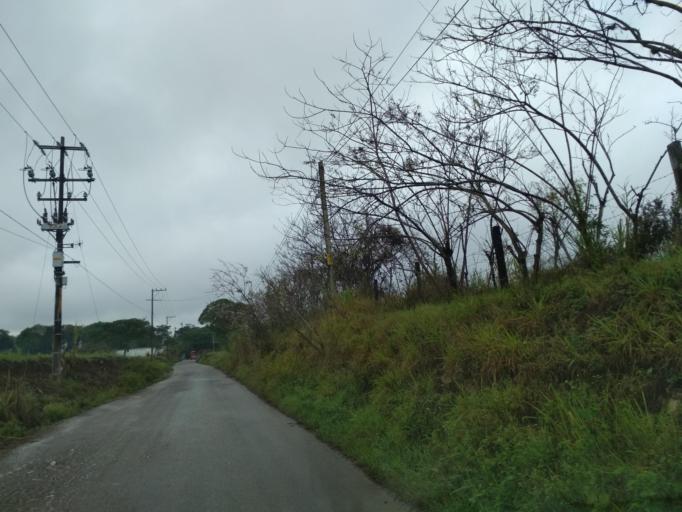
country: MX
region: Veracruz
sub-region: Amatlan de los Reyes
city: Centro de Readaptacion Social
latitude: 18.8366
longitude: -96.9387
